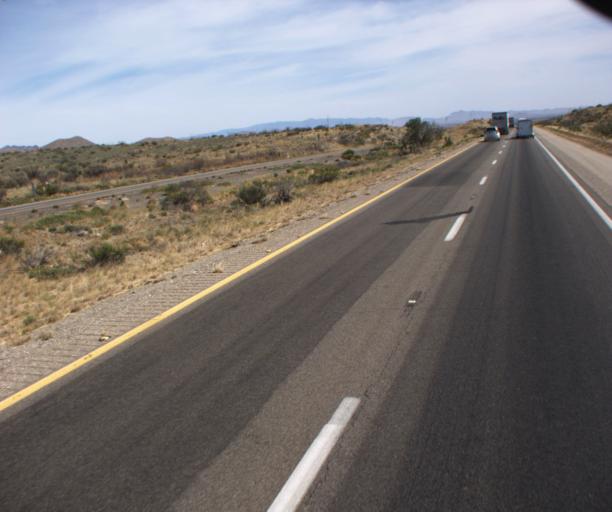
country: US
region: Arizona
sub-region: Cochise County
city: Willcox
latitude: 32.1318
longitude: -110.0077
